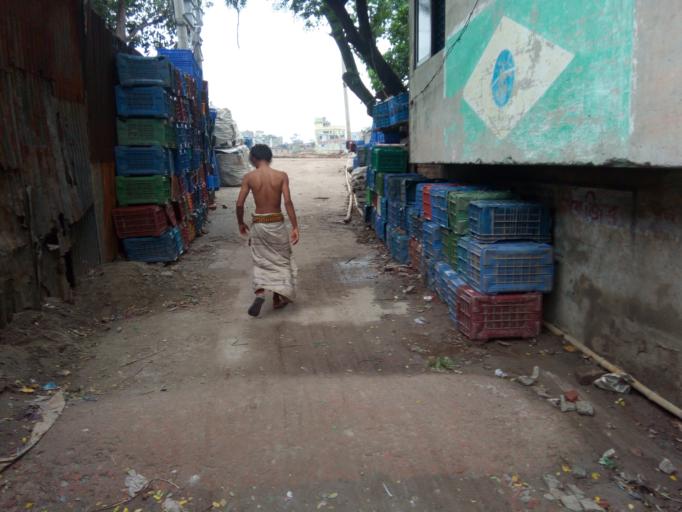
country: BD
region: Dhaka
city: Azimpur
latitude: 23.7158
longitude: 90.3801
